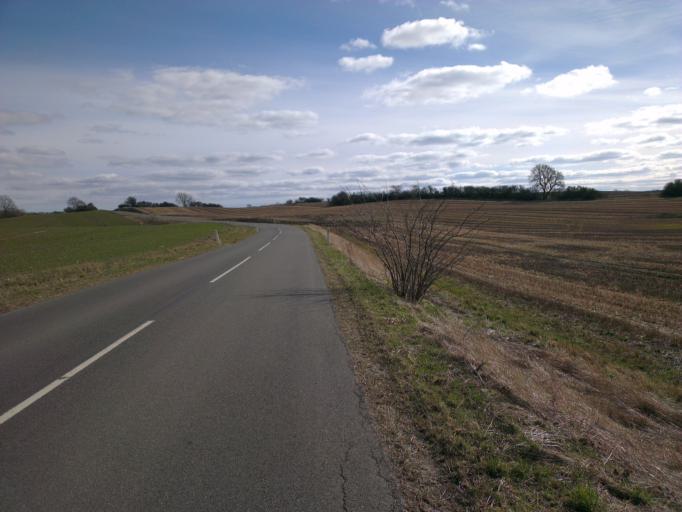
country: DK
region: Capital Region
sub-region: Frederikssund Kommune
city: Skibby
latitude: 55.7408
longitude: 12.0159
